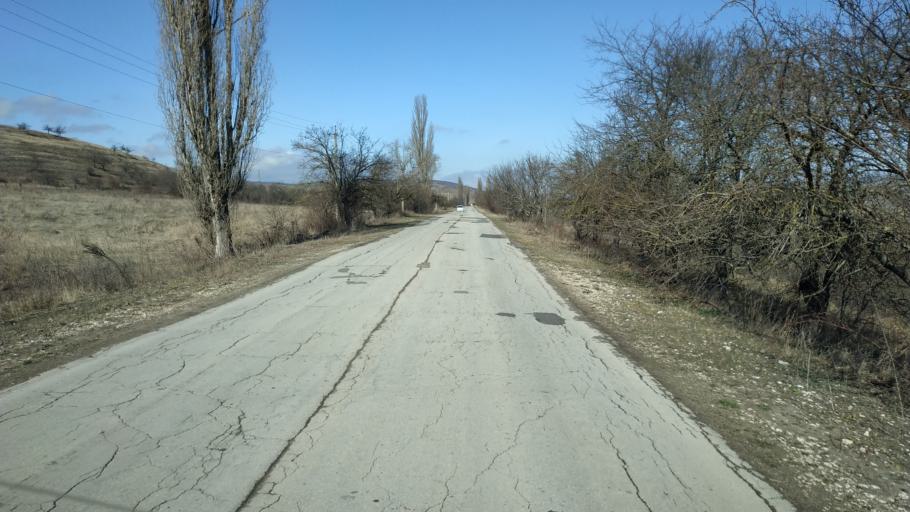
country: MD
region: Hincesti
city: Hincesti
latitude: 46.9870
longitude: 28.5585
